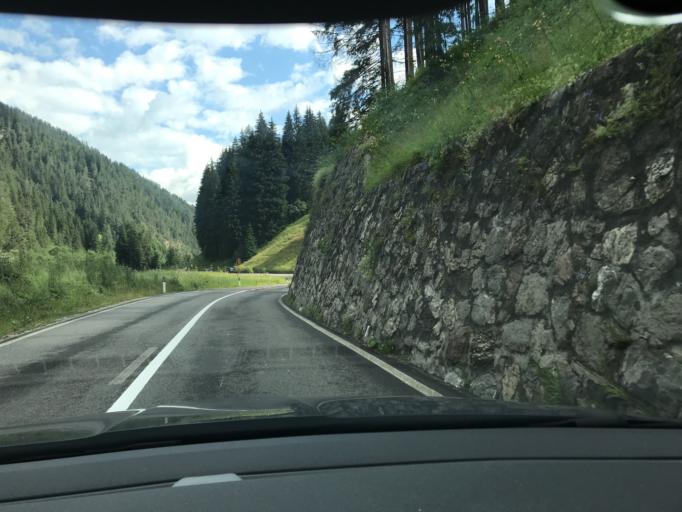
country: IT
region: Trentino-Alto Adige
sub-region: Bolzano
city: Badia
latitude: 46.6366
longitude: 11.9000
